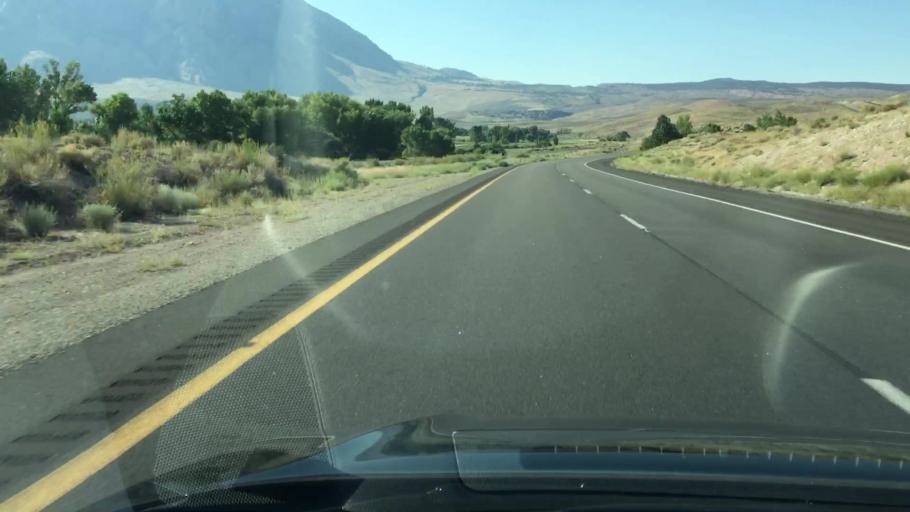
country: US
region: California
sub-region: Inyo County
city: West Bishop
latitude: 37.4374
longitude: -118.5688
